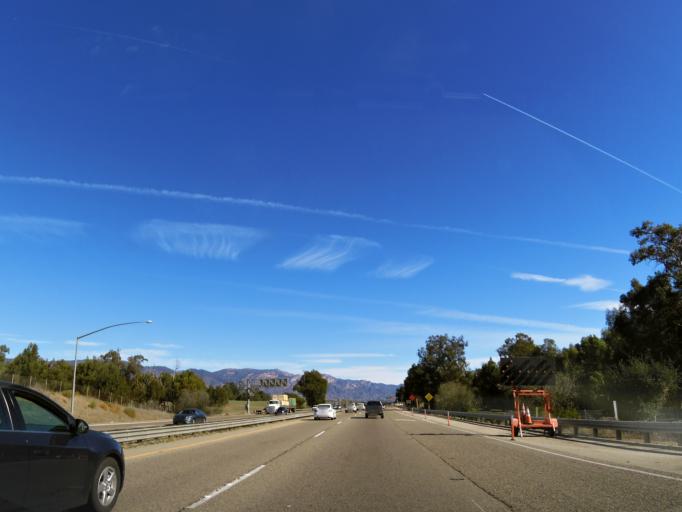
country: US
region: California
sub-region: Santa Barbara County
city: Isla Vista
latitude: 34.4358
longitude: -119.8625
